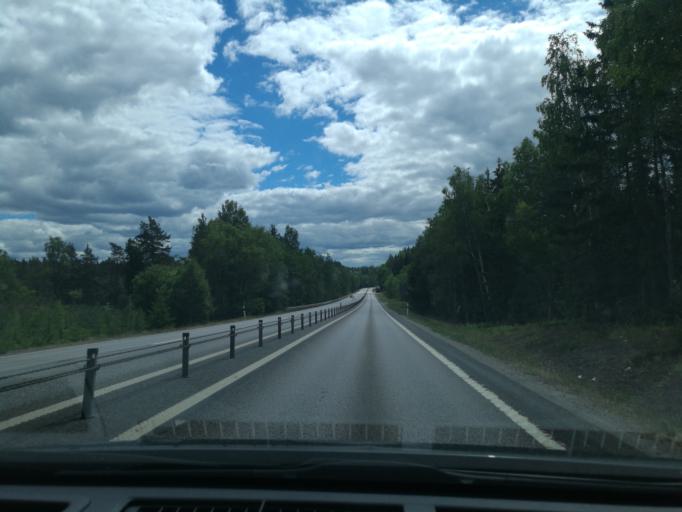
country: SE
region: OEstergoetland
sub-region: Norrkopings Kommun
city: Jursla
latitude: 58.7583
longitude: 16.1739
